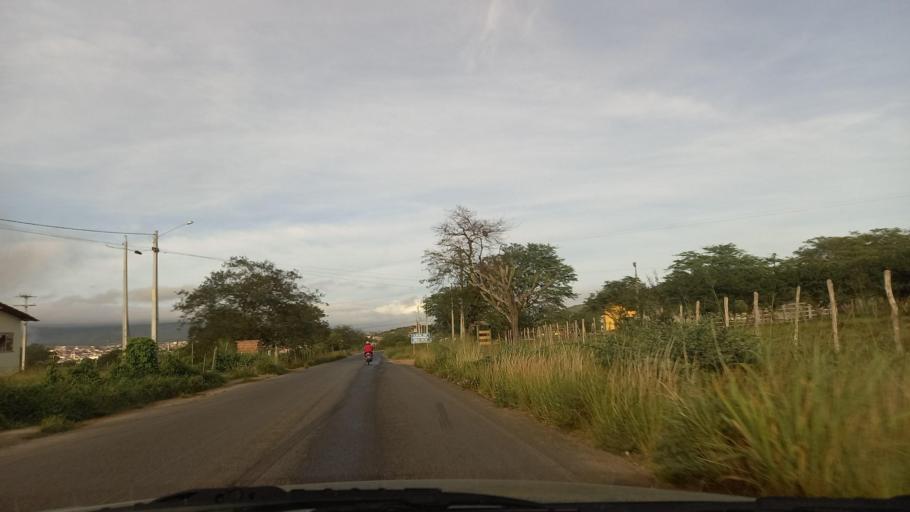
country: BR
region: Pernambuco
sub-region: Bezerros
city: Bezerros
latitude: -8.2160
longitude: -35.7446
